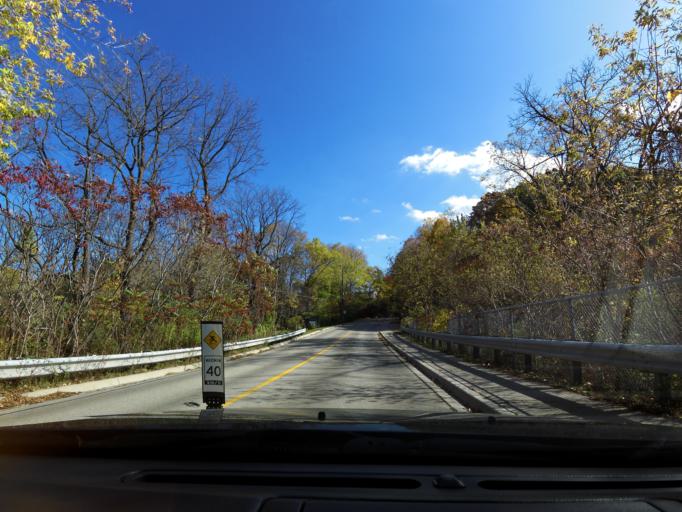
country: CA
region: Ontario
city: Hamilton
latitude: 43.3012
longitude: -79.8685
